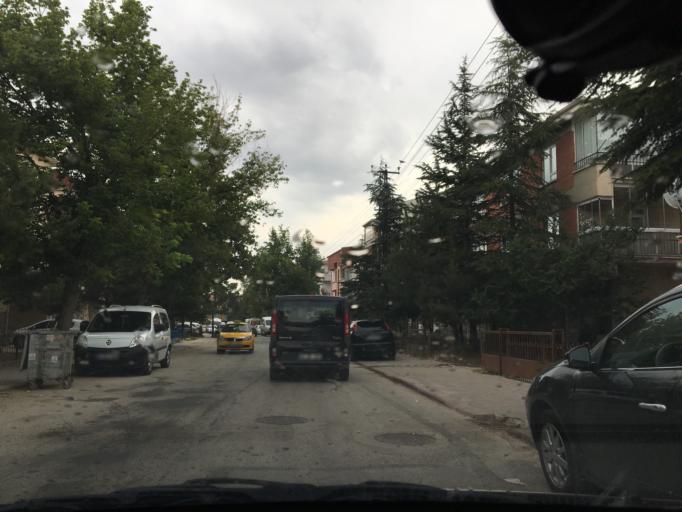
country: TR
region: Ankara
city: Ankara
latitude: 39.8810
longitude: 32.8313
